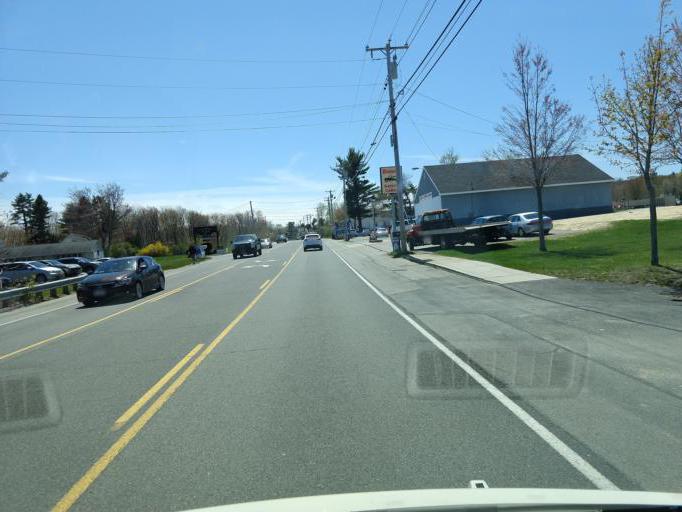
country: US
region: Maine
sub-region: York County
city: Ogunquit
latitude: 43.2782
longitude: -70.5958
